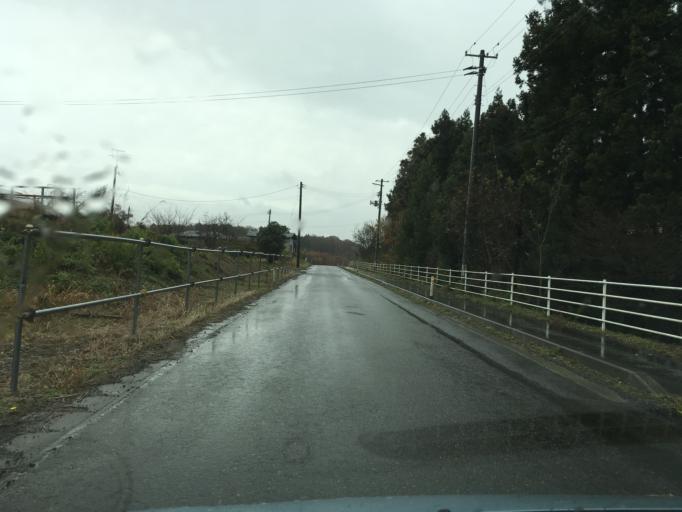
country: JP
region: Iwate
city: Ichinoseki
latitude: 38.7850
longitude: 141.2329
